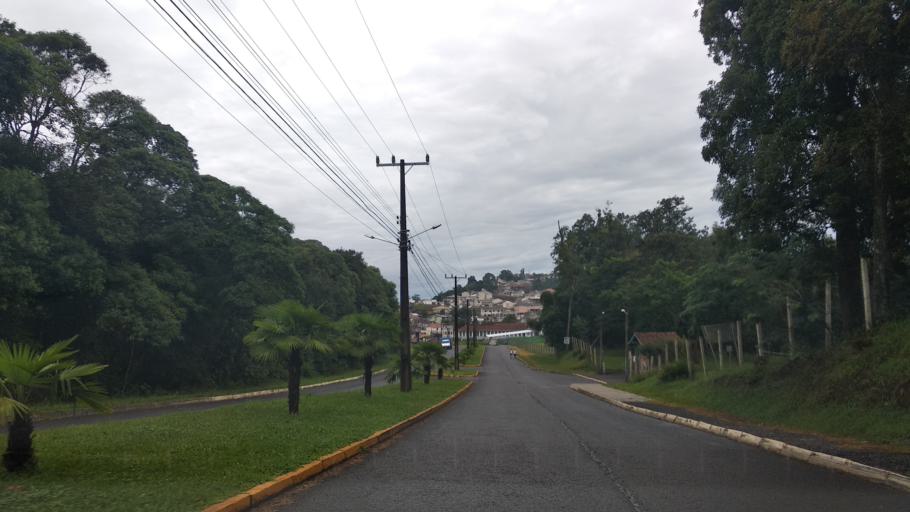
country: BR
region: Santa Catarina
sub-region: Videira
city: Videira
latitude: -26.9889
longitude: -51.1808
